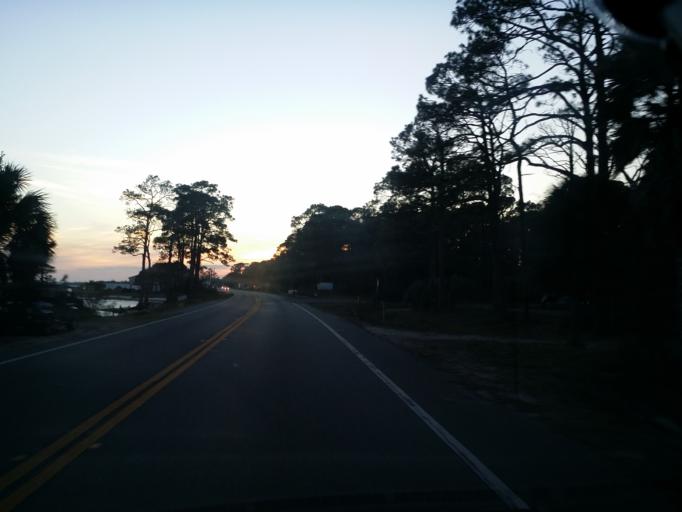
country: US
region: Florida
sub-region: Franklin County
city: Eastpoint
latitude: 29.7436
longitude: -84.8666
